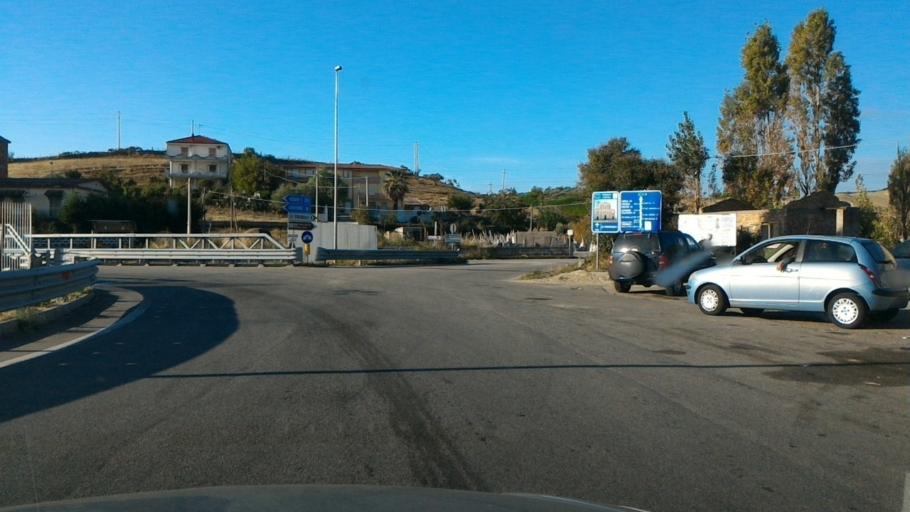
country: IT
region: Calabria
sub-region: Provincia di Crotone
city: Tronca
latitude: 39.2299
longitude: 17.1004
